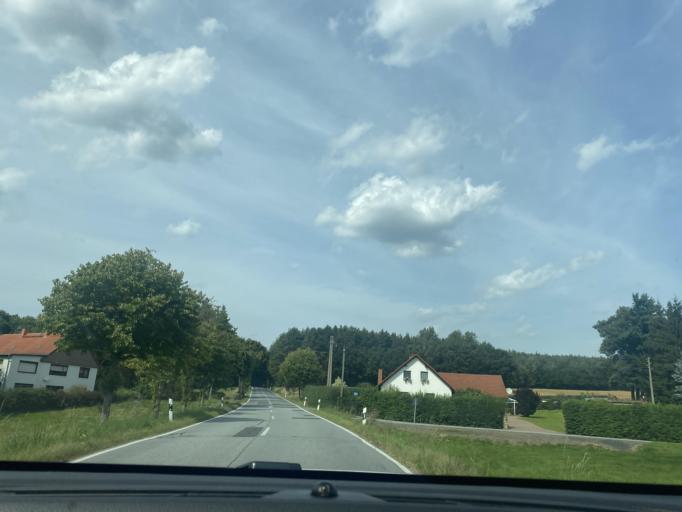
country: DE
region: Saxony
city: Grosshennersdorf
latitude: 51.0037
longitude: 14.7955
